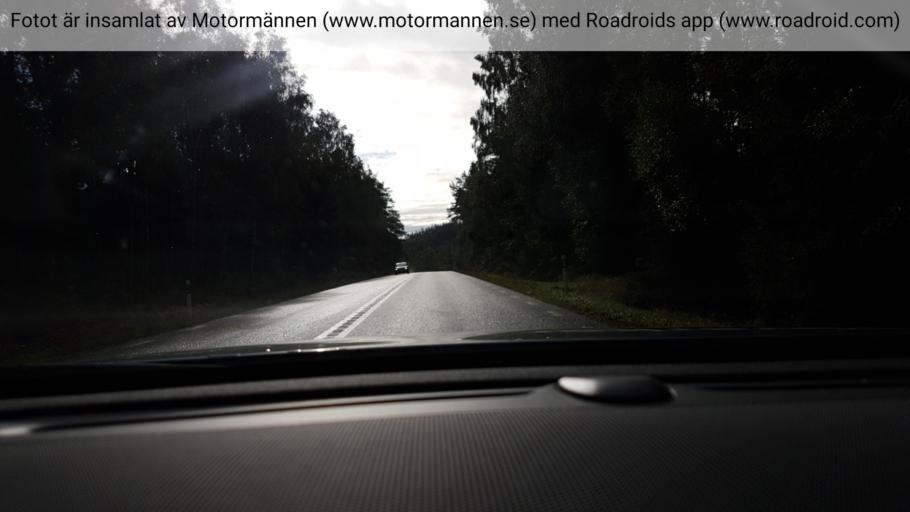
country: SE
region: Vaestra Goetaland
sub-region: Harryda Kommun
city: Ravlanda
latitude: 57.5818
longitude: 12.4915
